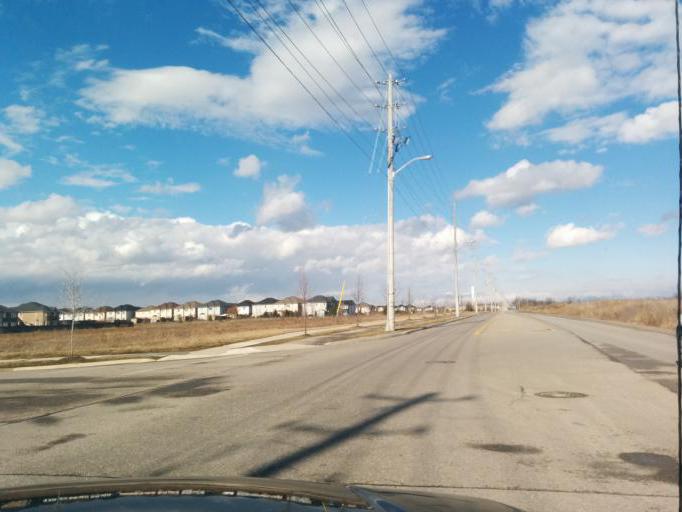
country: CA
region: Ontario
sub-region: Halton
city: Milton
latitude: 43.5003
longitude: -79.8444
